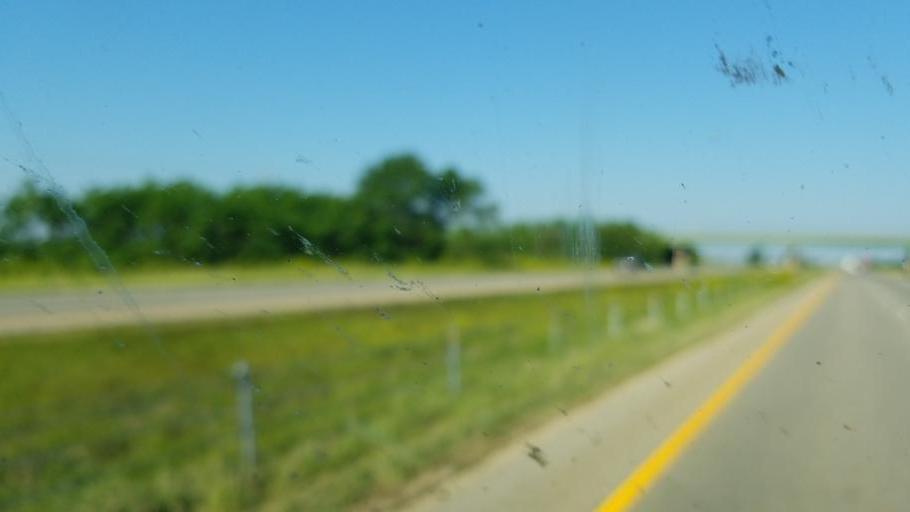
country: US
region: Illinois
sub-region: LaSalle County
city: Ottawa
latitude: 41.3685
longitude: -88.8922
